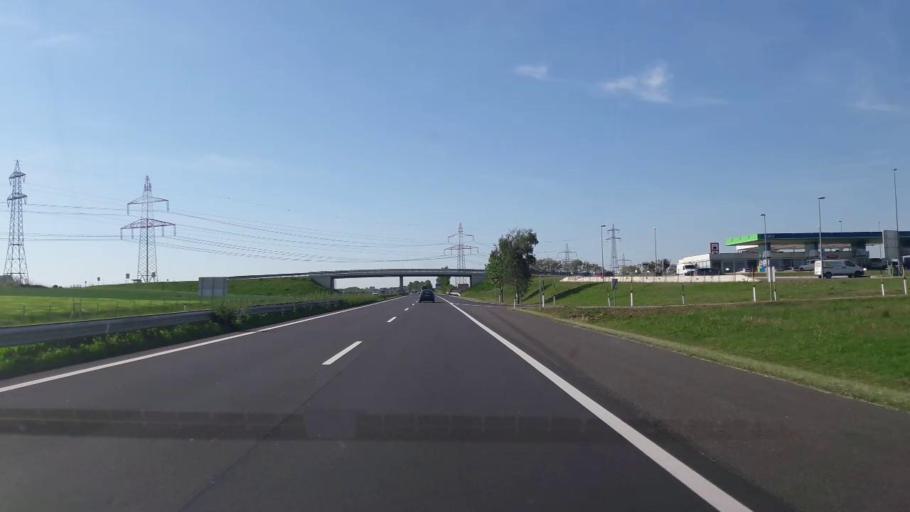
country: AT
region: Burgenland
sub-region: Eisenstadt-Umgebung
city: Hornstein
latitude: 47.8792
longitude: 16.4156
